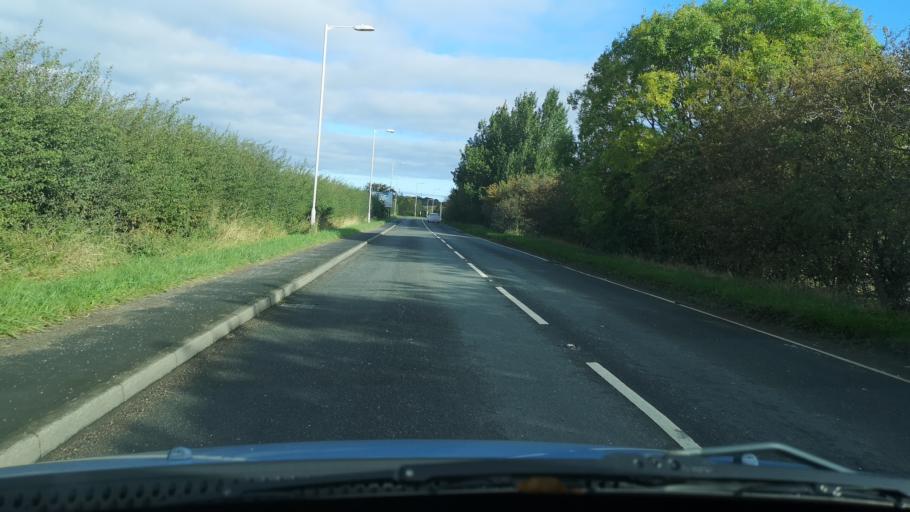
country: GB
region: England
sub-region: City and Borough of Wakefield
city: Featherstone
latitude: 53.6793
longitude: -1.3775
